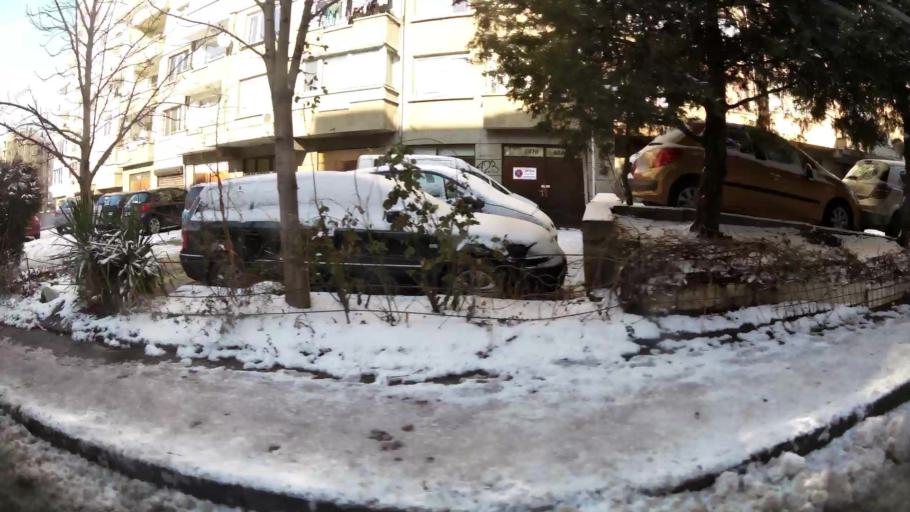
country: BG
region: Sofia-Capital
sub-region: Stolichna Obshtina
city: Sofia
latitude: 42.6642
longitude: 23.3548
